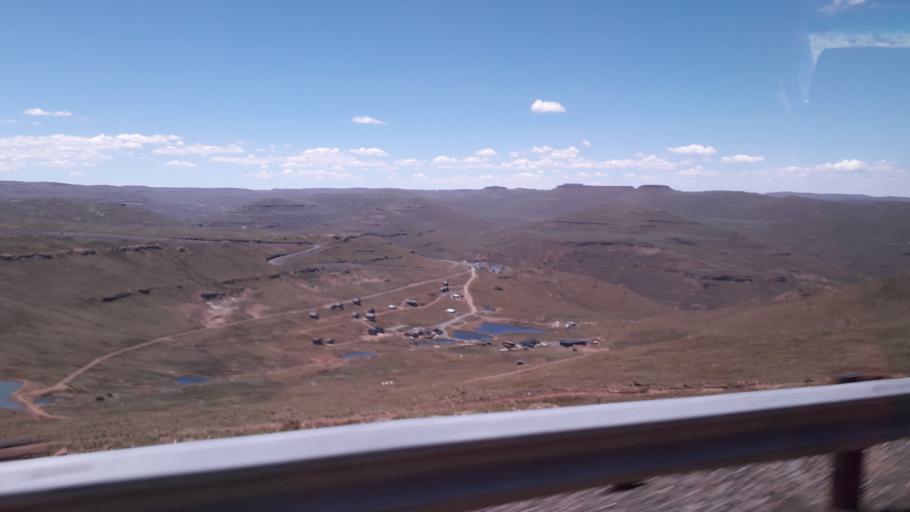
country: ZA
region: Orange Free State
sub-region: Thabo Mofutsanyana District Municipality
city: Phuthaditjhaba
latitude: -28.8132
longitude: 28.7223
